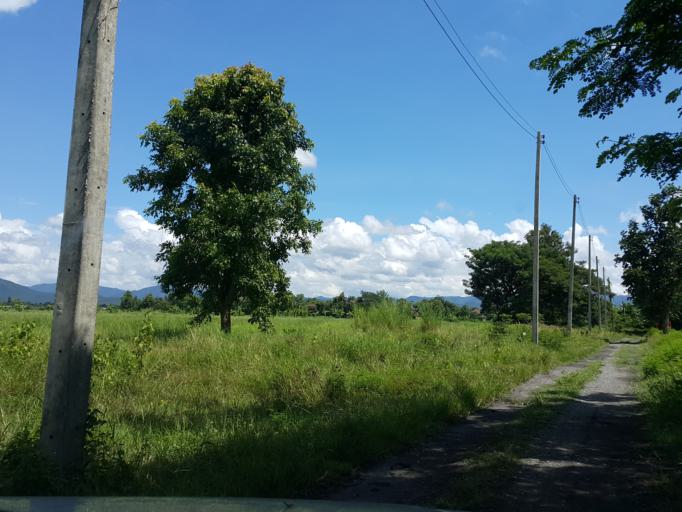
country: TH
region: Chiang Mai
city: San Kamphaeng
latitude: 18.7650
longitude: 99.1220
